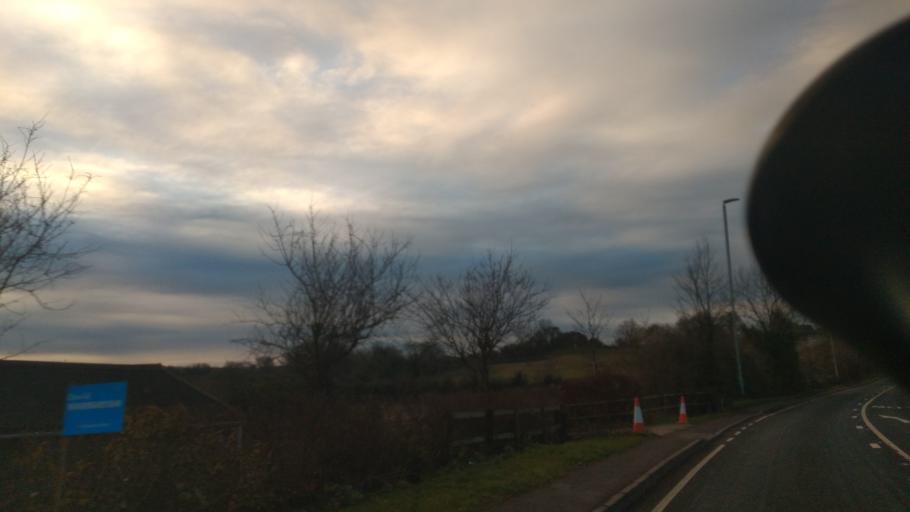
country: GB
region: England
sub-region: Somerset
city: Frome
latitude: 51.2492
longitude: -2.3077
